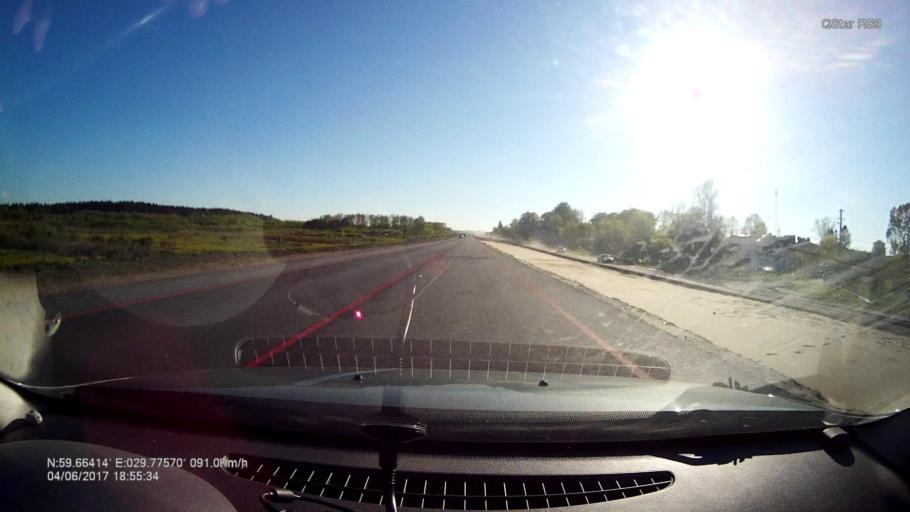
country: RU
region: Leningrad
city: Kipen'
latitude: 59.6641
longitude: 29.7754
